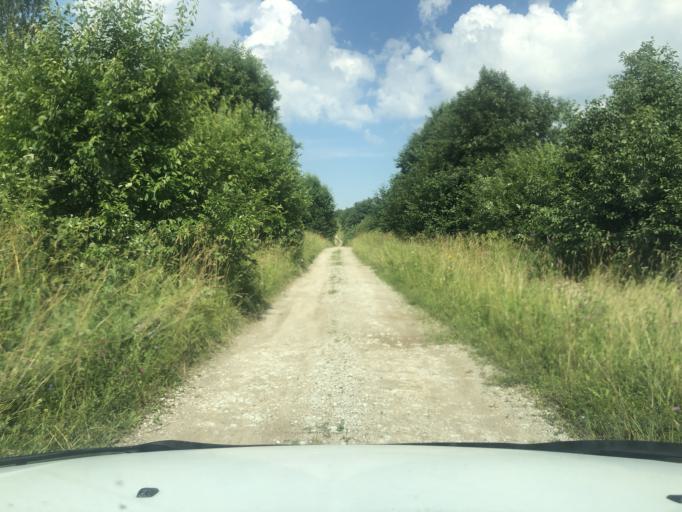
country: RU
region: Jaroslavl
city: Pereslavl'-Zalesskiy
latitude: 57.0411
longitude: 38.8730
